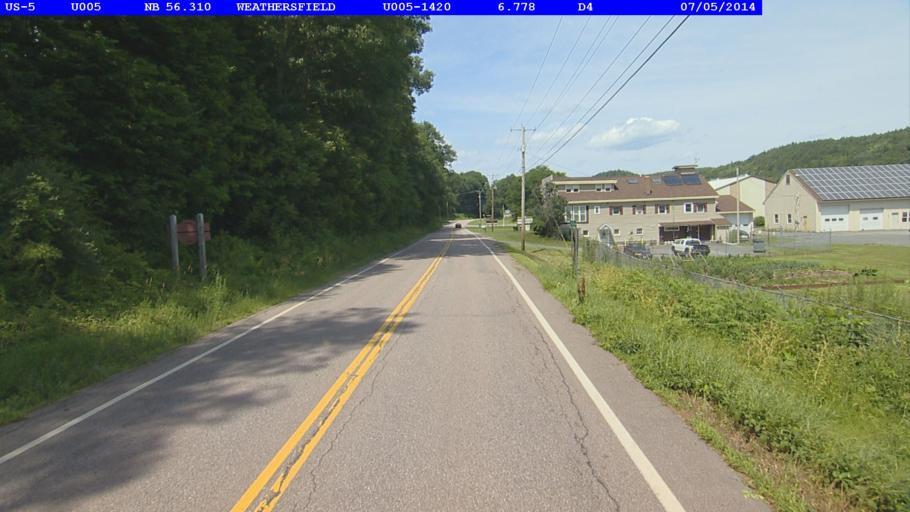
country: US
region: Vermont
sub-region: Windsor County
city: Windsor
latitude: 43.4289
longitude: -72.3992
